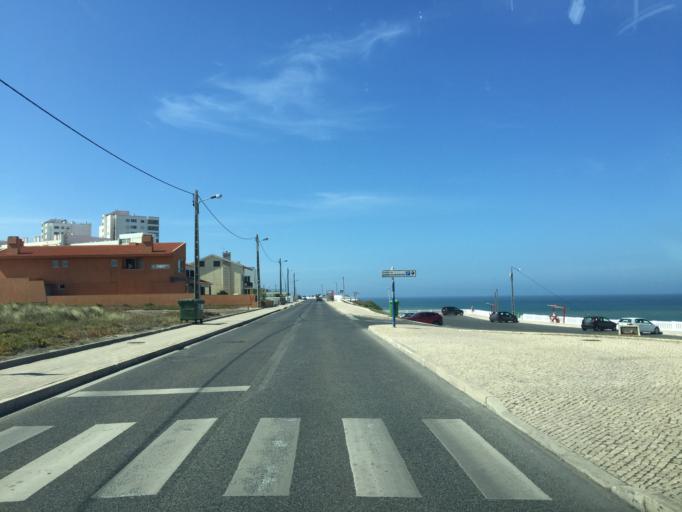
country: PT
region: Lisbon
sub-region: Torres Vedras
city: Silveira
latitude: 39.1424
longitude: -9.3754
